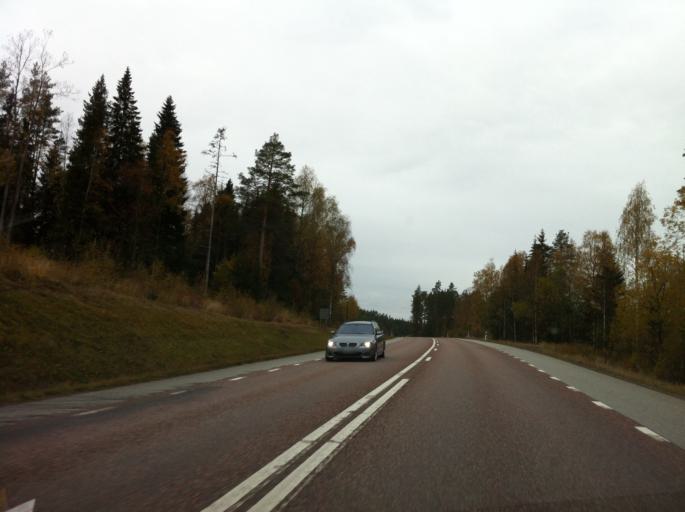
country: SE
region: Dalarna
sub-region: Ludvika Kommun
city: Grangesberg
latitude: 59.9967
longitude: 15.0126
